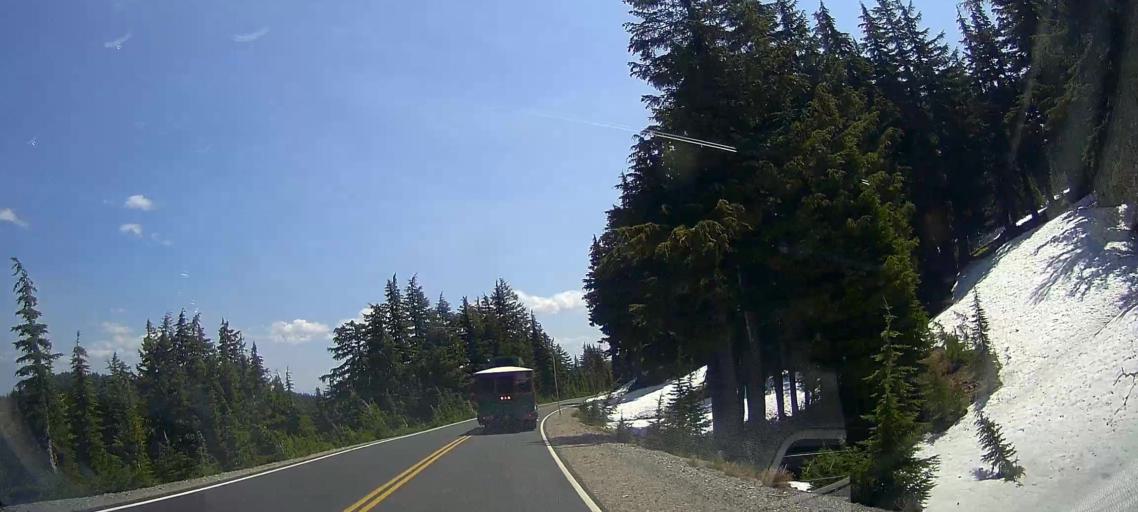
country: US
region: Oregon
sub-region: Jackson County
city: Shady Cove
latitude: 42.9823
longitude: -122.1342
